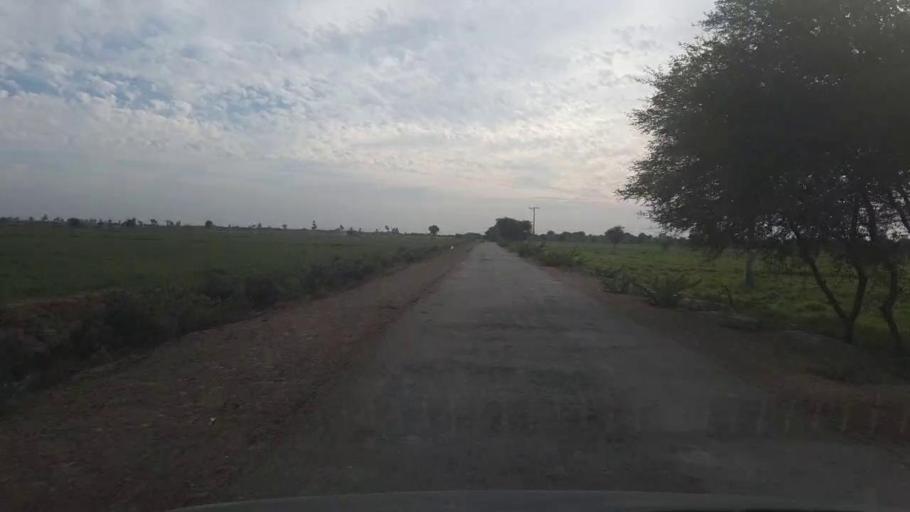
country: PK
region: Sindh
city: Samaro
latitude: 25.3282
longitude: 69.2375
